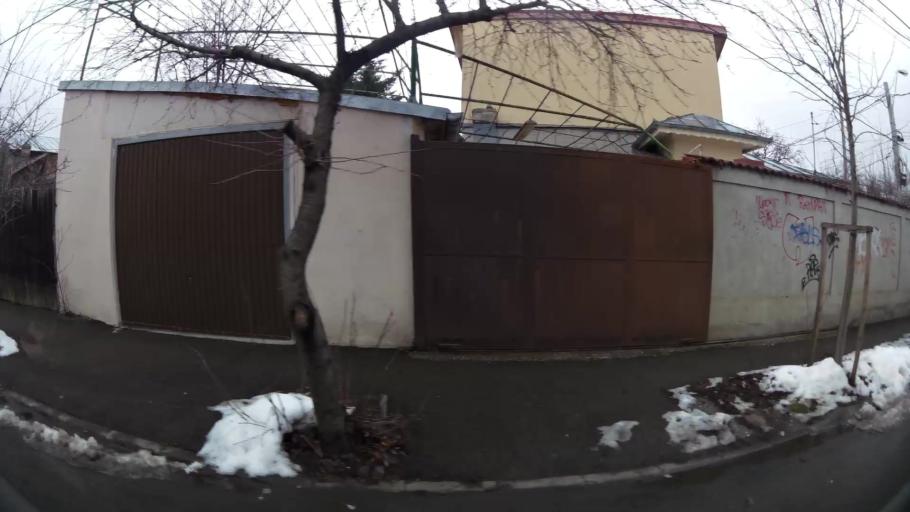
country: RO
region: Ilfov
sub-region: Comuna Chiajna
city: Rosu
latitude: 44.4887
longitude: 26.0285
